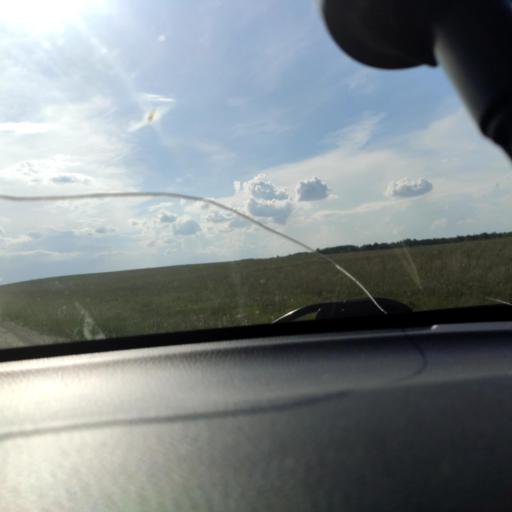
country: RU
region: Tatarstan
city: Verkhniy Uslon
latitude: 55.6434
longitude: 48.9113
